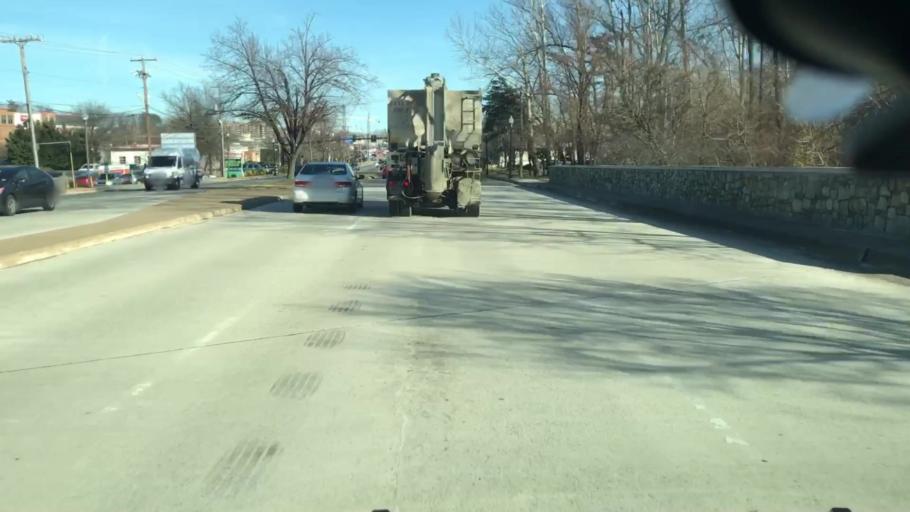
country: US
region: Virginia
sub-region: Fairfax County
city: Oakton
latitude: 38.8637
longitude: -77.2832
